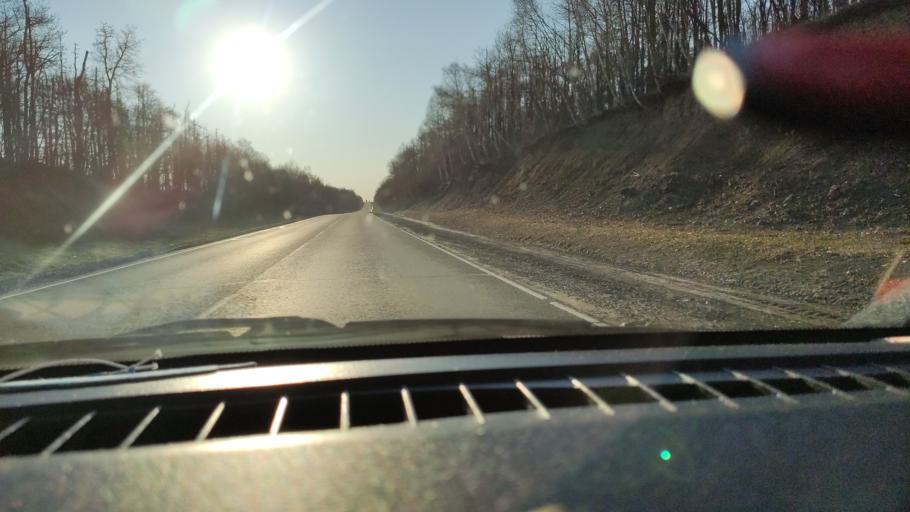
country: RU
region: Saratov
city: Vol'sk
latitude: 52.1111
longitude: 47.3406
